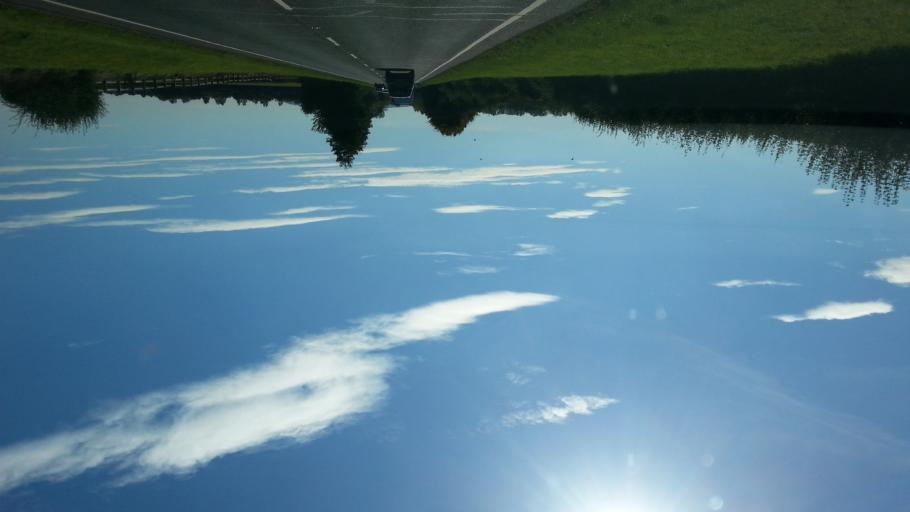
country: GB
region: England
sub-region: Telford and Wrekin
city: Oakengates
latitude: 52.7310
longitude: -2.4257
